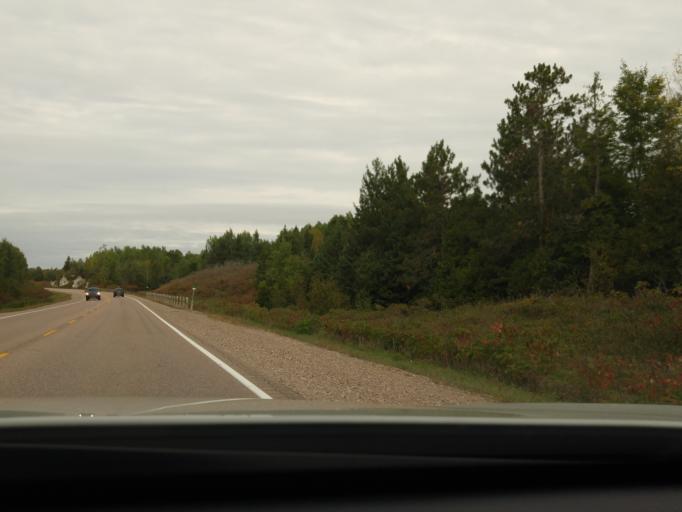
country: CA
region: Ontario
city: Renfrew
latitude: 45.5625
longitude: -76.7519
